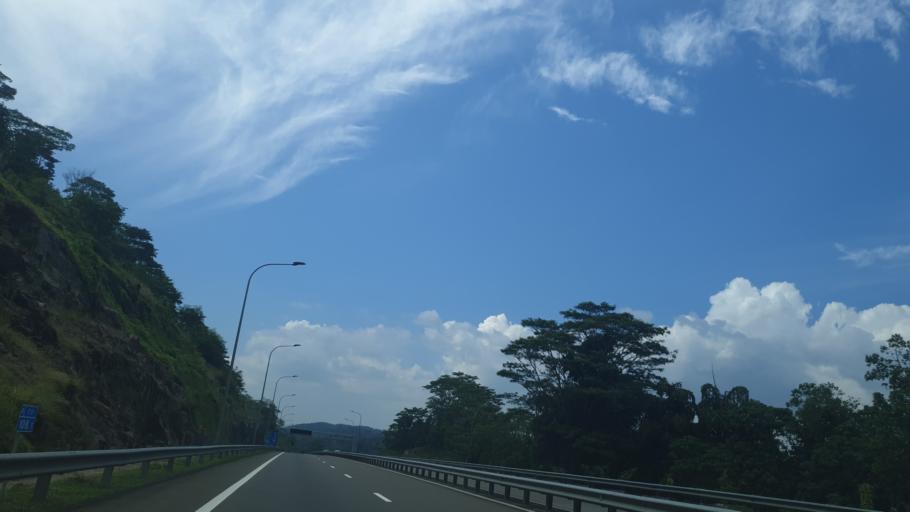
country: LK
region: Southern
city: Weligama
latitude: 6.0335
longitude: 80.3715
